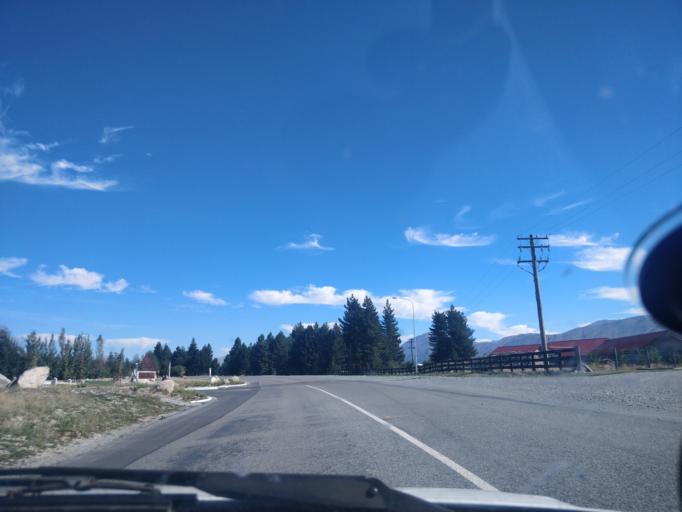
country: NZ
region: Otago
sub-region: Queenstown-Lakes District
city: Wanaka
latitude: -44.2650
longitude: 170.0808
